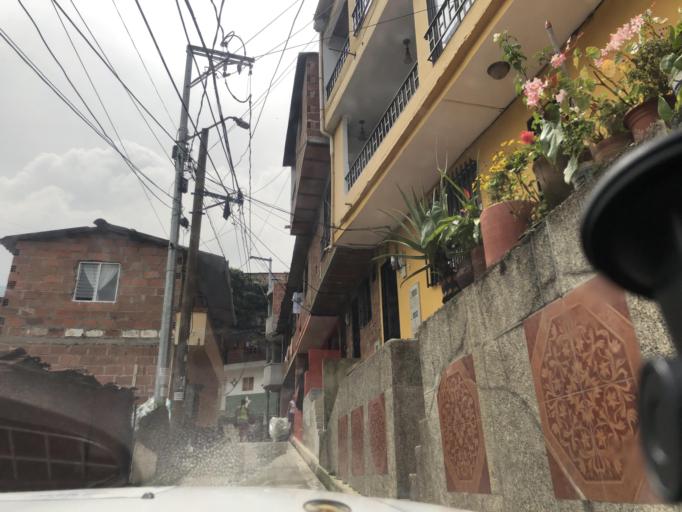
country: CO
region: Antioquia
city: Bello
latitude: 6.3302
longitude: -75.5357
